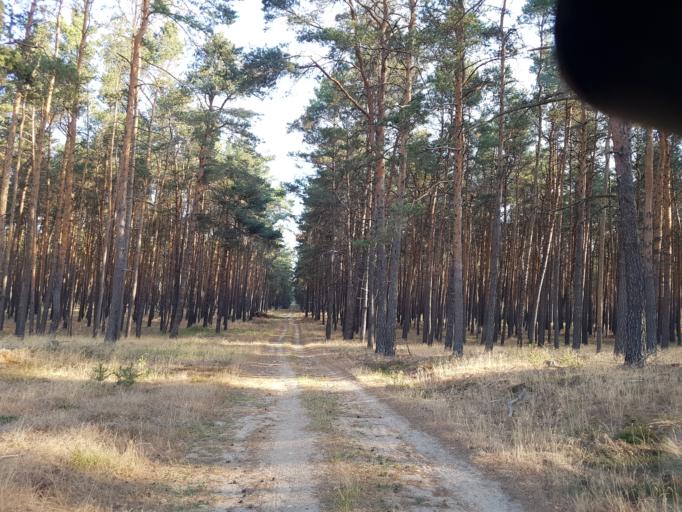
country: DE
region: Brandenburg
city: Niedergorsdorf
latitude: 52.0273
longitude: 12.9249
